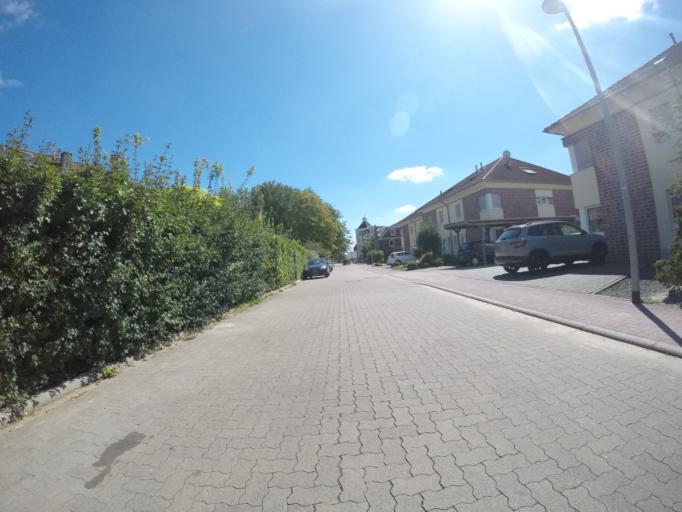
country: DE
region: North Rhine-Westphalia
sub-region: Regierungsbezirk Dusseldorf
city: Bocholt
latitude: 51.8376
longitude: 6.5918
